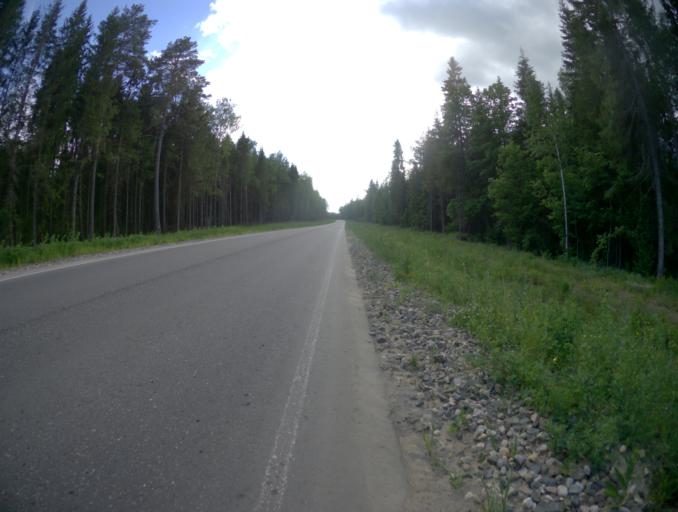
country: RU
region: Ivanovo
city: Kitovo
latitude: 56.8038
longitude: 41.1807
